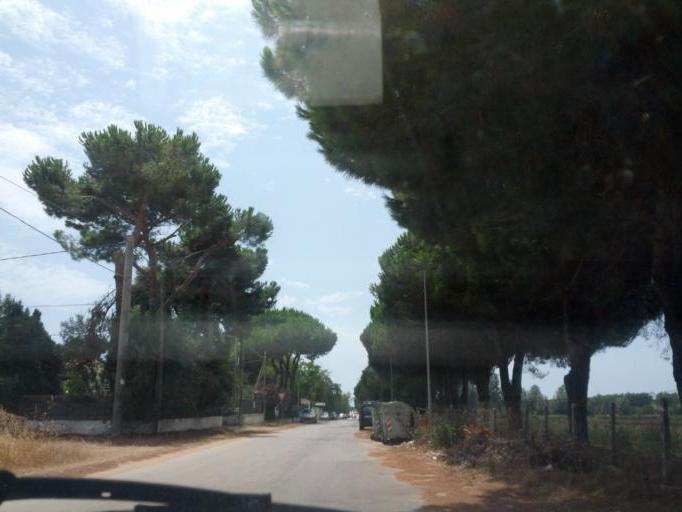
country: IT
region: Latium
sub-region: Provincia di Latina
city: Sperlonga
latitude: 41.2844
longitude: 13.3887
